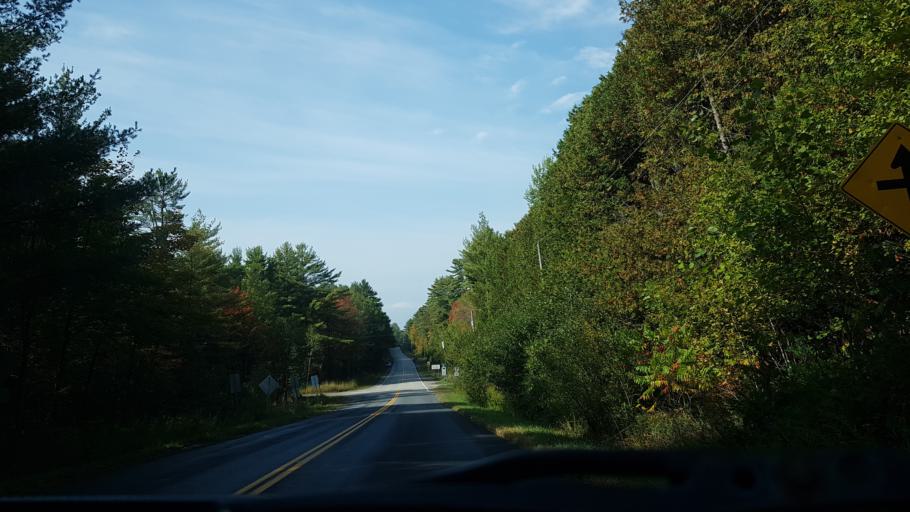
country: CA
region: Ontario
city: Gravenhurst
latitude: 44.7838
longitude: -79.2560
